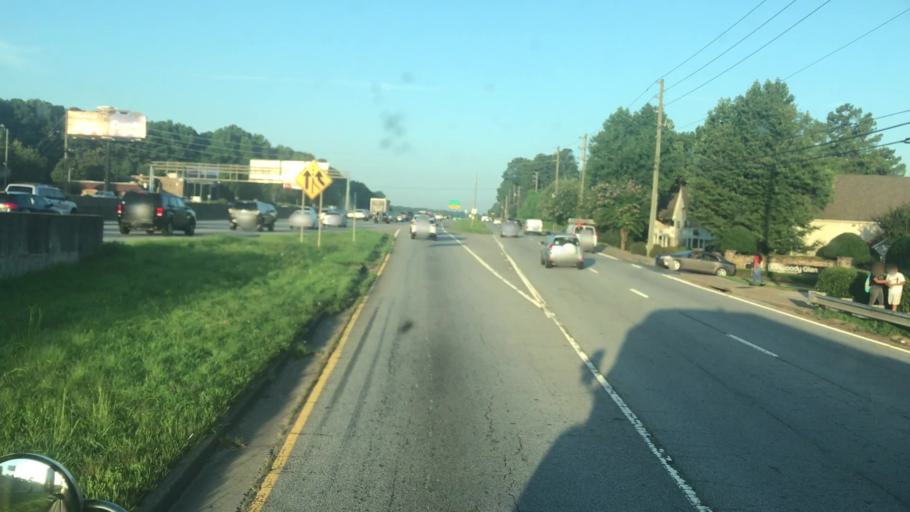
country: US
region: Georgia
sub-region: DeKalb County
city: Doraville
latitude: 33.9293
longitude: -84.2694
